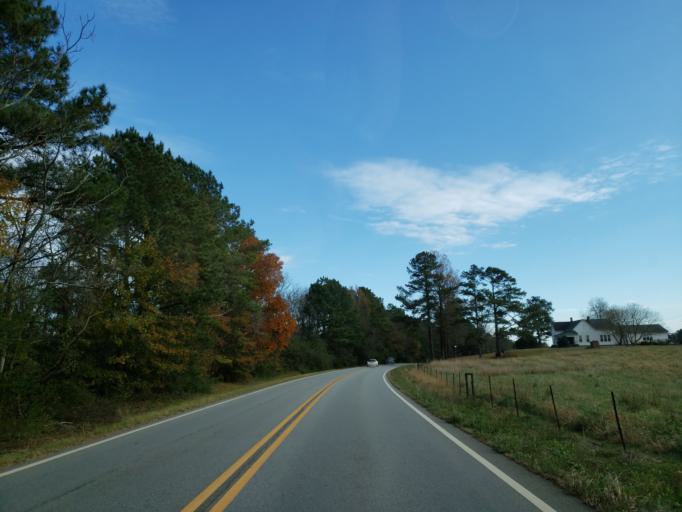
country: US
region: Georgia
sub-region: Monroe County
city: Forsyth
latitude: 32.9787
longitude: -83.8744
